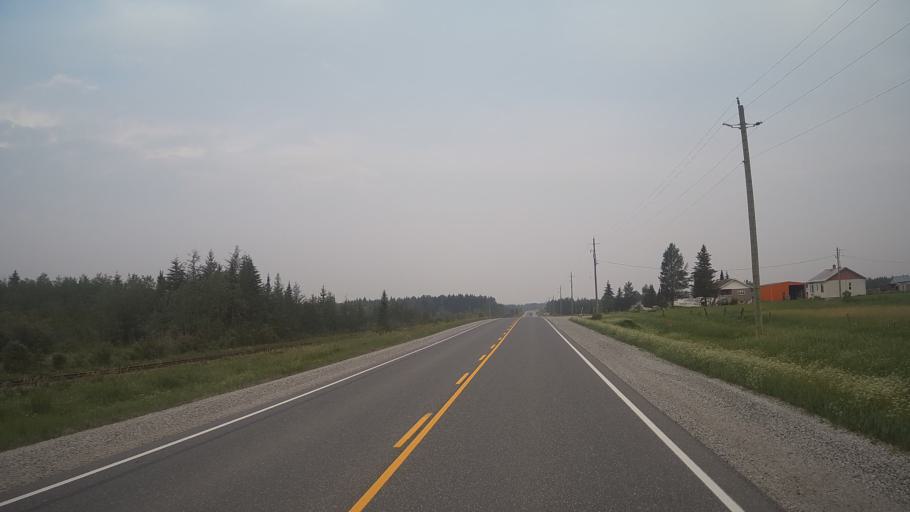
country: CA
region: Ontario
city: Hearst
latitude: 49.6763
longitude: -83.5746
